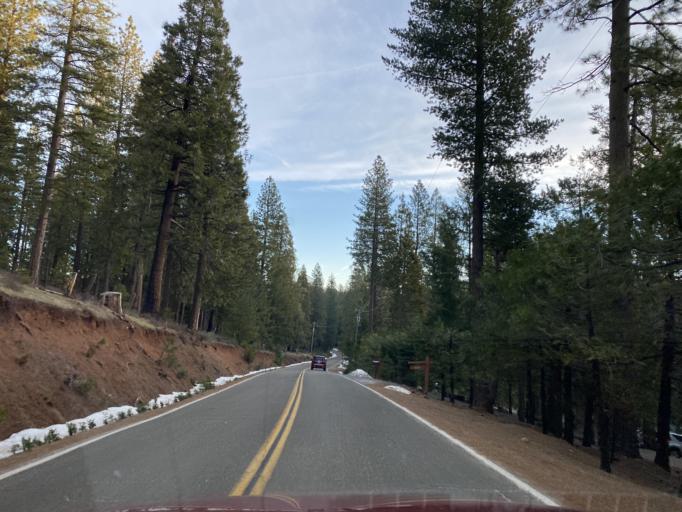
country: US
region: California
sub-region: Amador County
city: Pioneer
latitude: 38.5051
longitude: -120.5158
